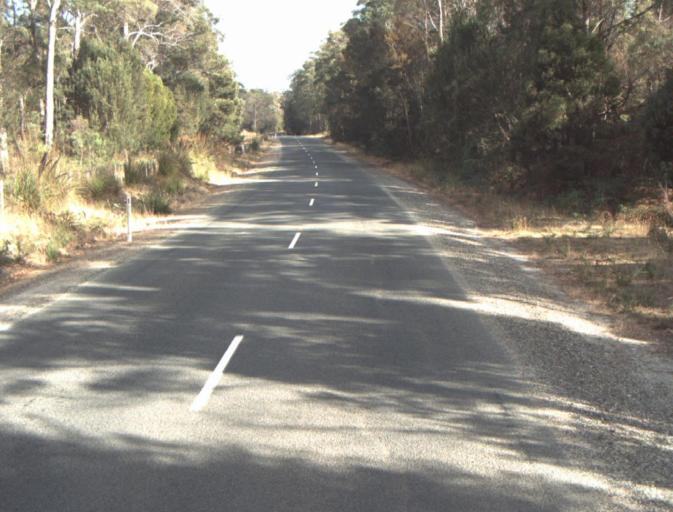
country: AU
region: Tasmania
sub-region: Dorset
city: Bridport
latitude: -41.1266
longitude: 147.2111
